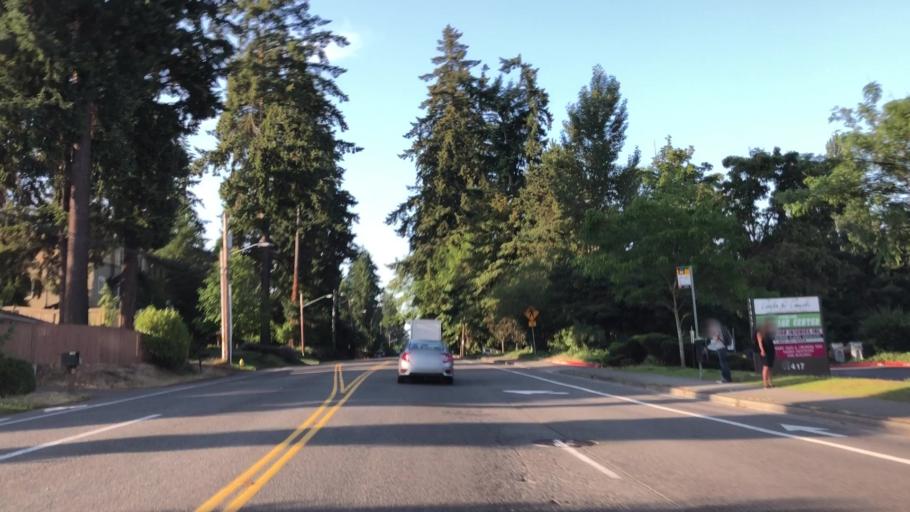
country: US
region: Washington
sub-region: King County
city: Kingsgate
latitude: 47.7027
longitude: -122.1759
